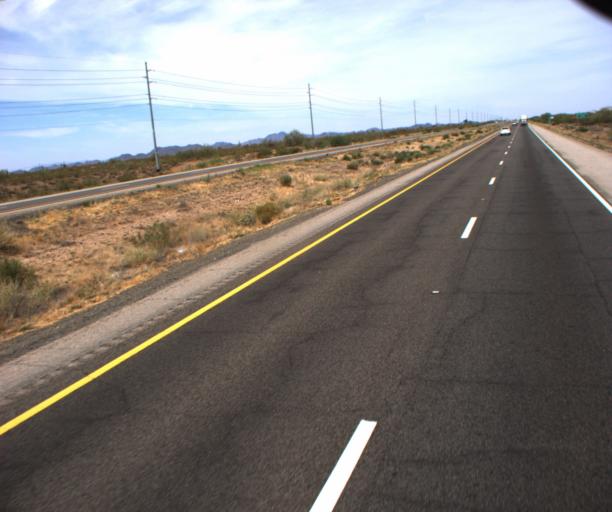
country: US
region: Arizona
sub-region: Maricopa County
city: Wickenburg
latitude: 33.8033
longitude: -112.5610
